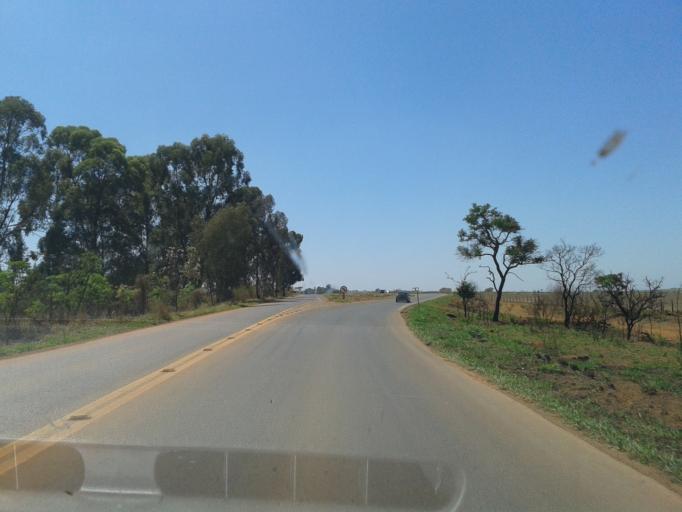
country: BR
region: Minas Gerais
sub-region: Araxa
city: Araxa
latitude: -19.4175
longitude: -47.2924
